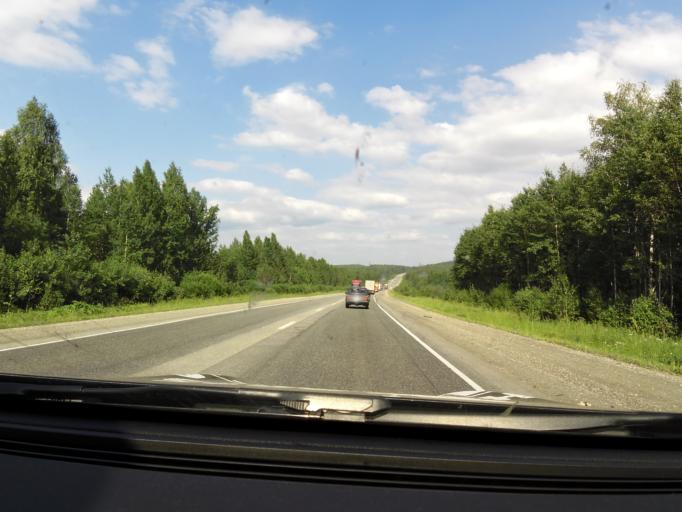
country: RU
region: Sverdlovsk
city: Talitsa
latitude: 56.8440
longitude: 60.0160
